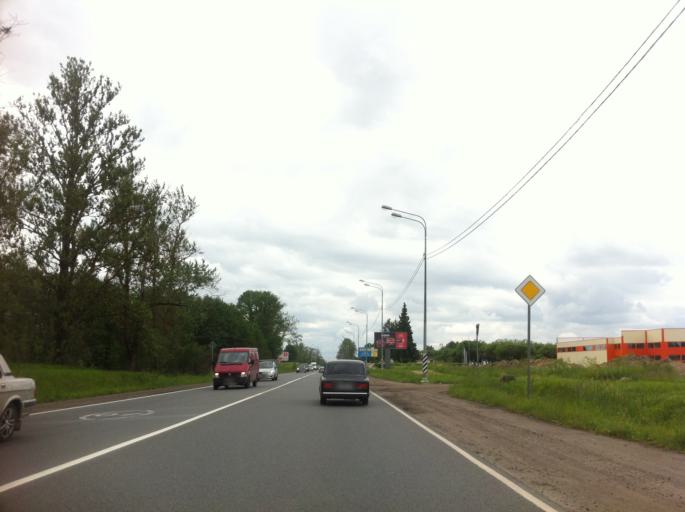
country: RU
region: Leningrad
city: Maloye Verevo
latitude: 59.6119
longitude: 30.1715
